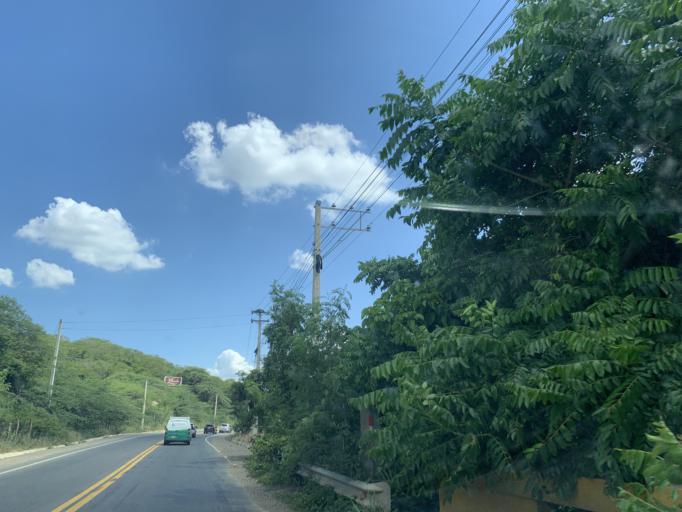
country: DO
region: Santiago
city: Villa Bisono
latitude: 19.5825
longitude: -70.8454
